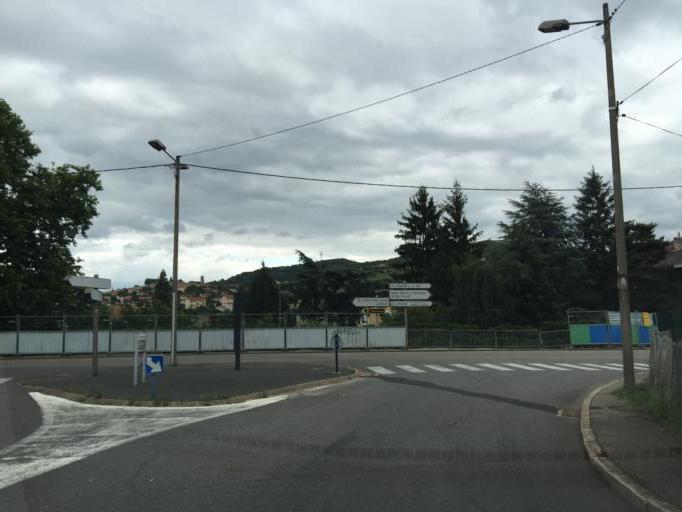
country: FR
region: Rhone-Alpes
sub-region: Departement de la Loire
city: Saint-Chamond
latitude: 45.4625
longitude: 4.5033
